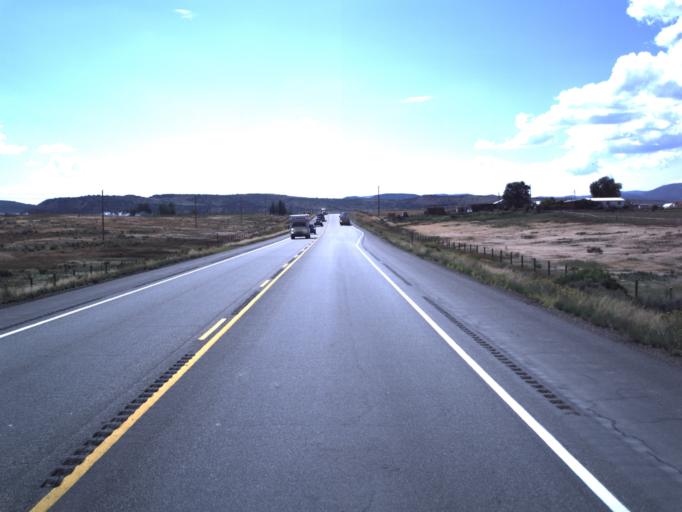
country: US
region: Utah
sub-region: Duchesne County
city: Duchesne
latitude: 40.2124
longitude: -110.8450
